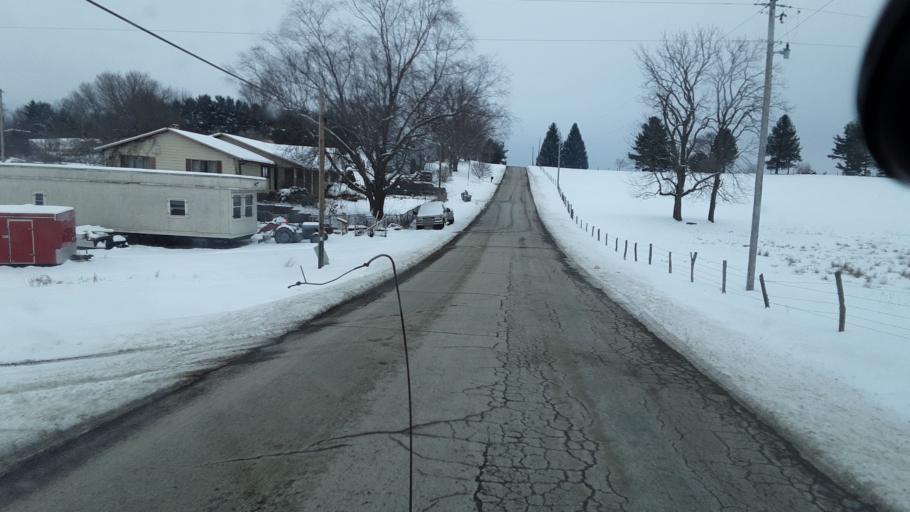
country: US
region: Ohio
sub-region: Muskingum County
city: Zanesville
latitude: 39.9344
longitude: -82.1777
